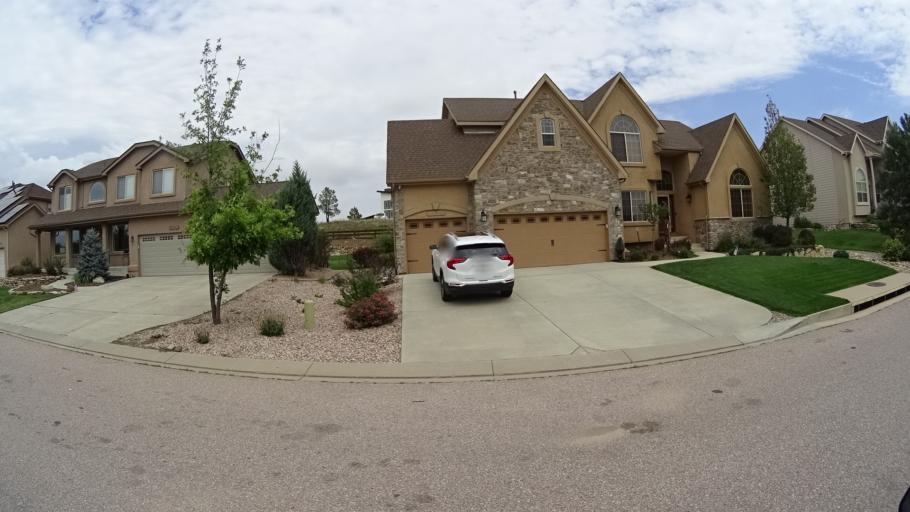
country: US
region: Colorado
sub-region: El Paso County
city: Gleneagle
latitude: 39.0160
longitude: -104.8005
